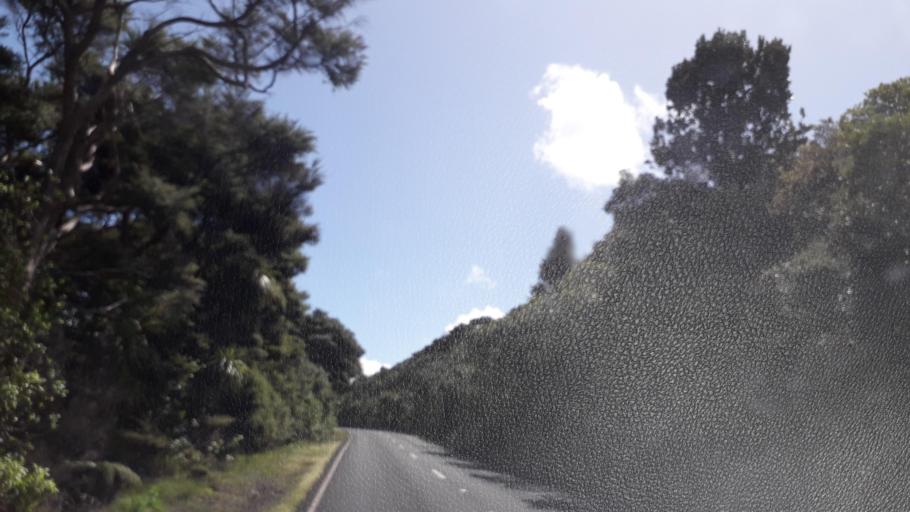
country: NZ
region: Northland
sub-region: Far North District
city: Paihia
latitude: -35.2477
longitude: 174.2576
